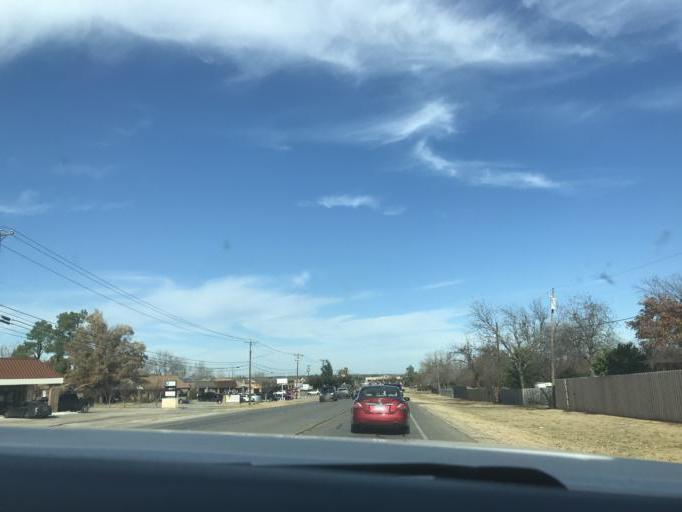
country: US
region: Texas
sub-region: Erath County
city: Stephenville
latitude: 32.2209
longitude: -98.2363
